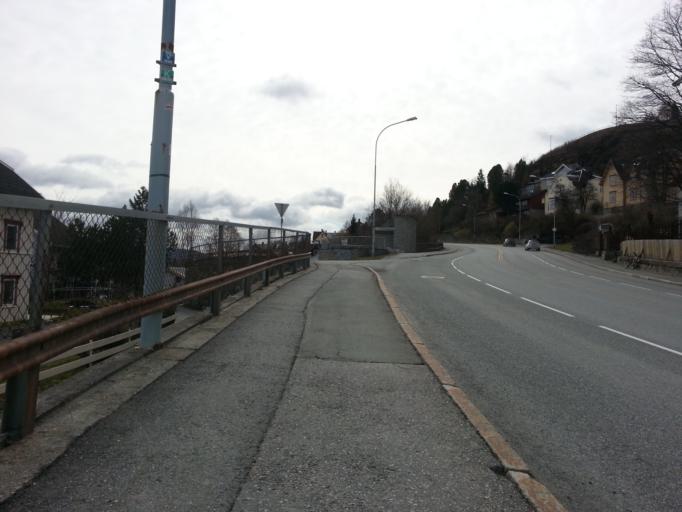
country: NO
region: Sor-Trondelag
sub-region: Trondheim
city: Trondheim
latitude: 63.4234
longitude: 10.3724
